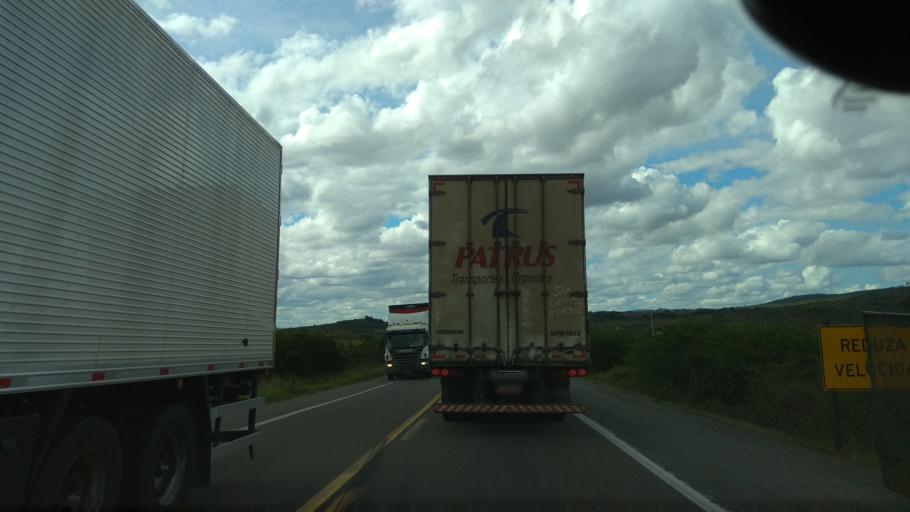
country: BR
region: Bahia
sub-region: Santa Ines
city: Santa Ines
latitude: -12.9884
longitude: -39.9455
